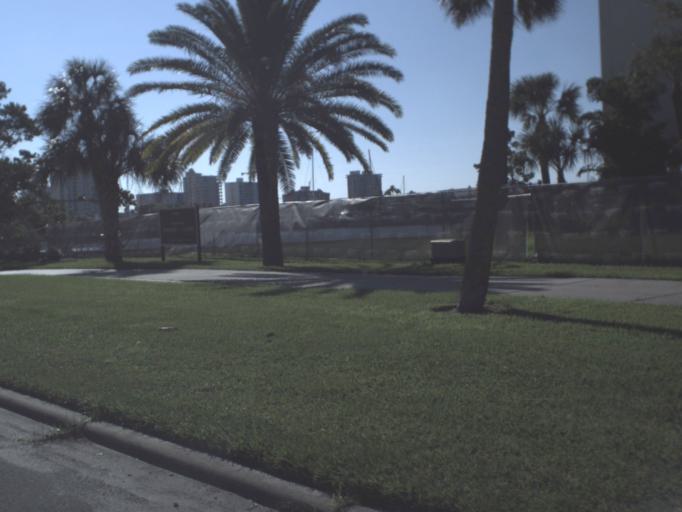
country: US
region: Florida
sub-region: Sarasota County
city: Sarasota
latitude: 27.3357
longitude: -82.5495
